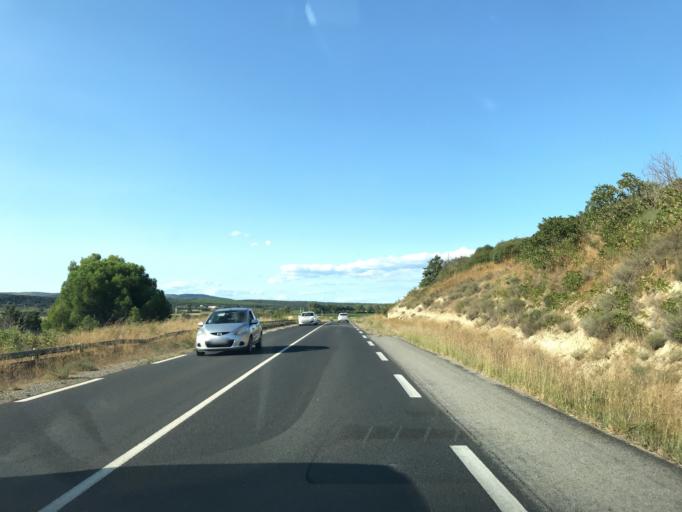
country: FR
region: Languedoc-Roussillon
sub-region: Departement de l'Herault
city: Montbazin
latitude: 43.5059
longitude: 3.6842
